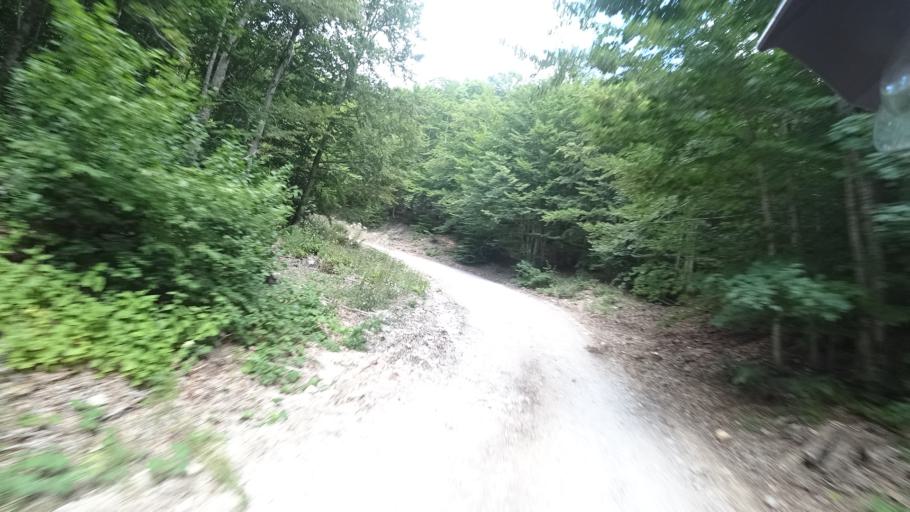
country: BA
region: Federation of Bosnia and Herzegovina
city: Orasac
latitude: 44.5732
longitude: 15.8556
